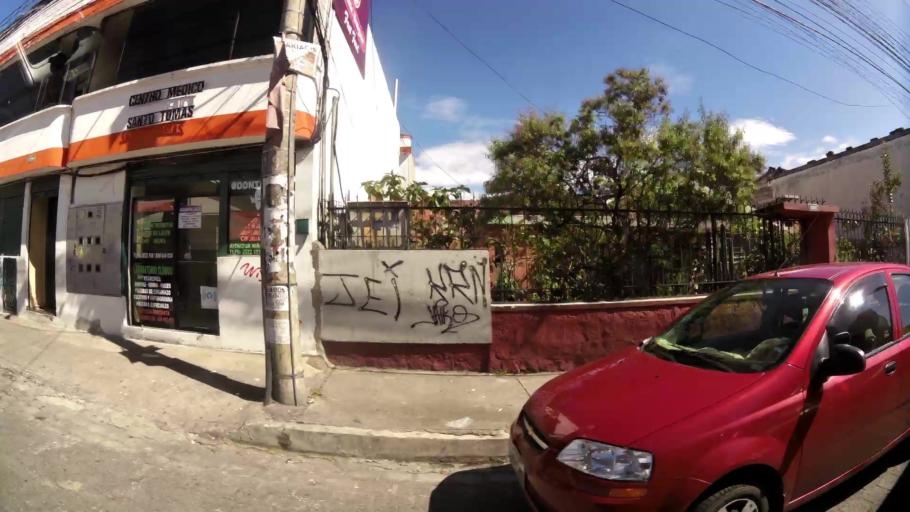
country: EC
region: Pichincha
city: Quito
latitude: -0.2764
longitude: -78.5549
